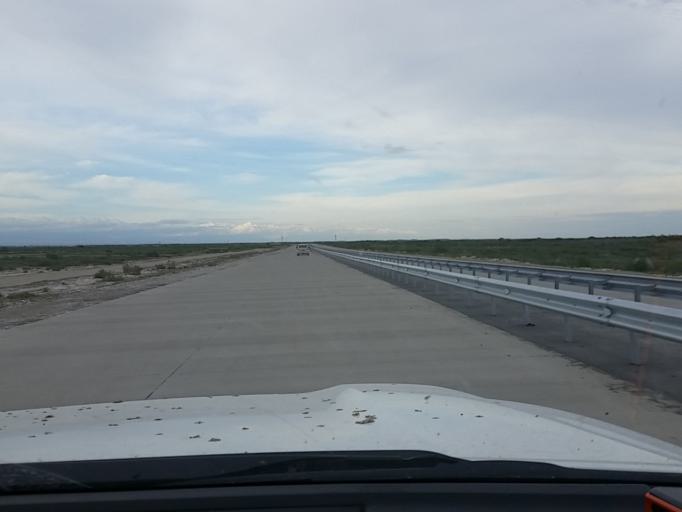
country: KZ
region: Almaty Oblysy
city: Zharkent
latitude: 44.0507
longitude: 79.9984
